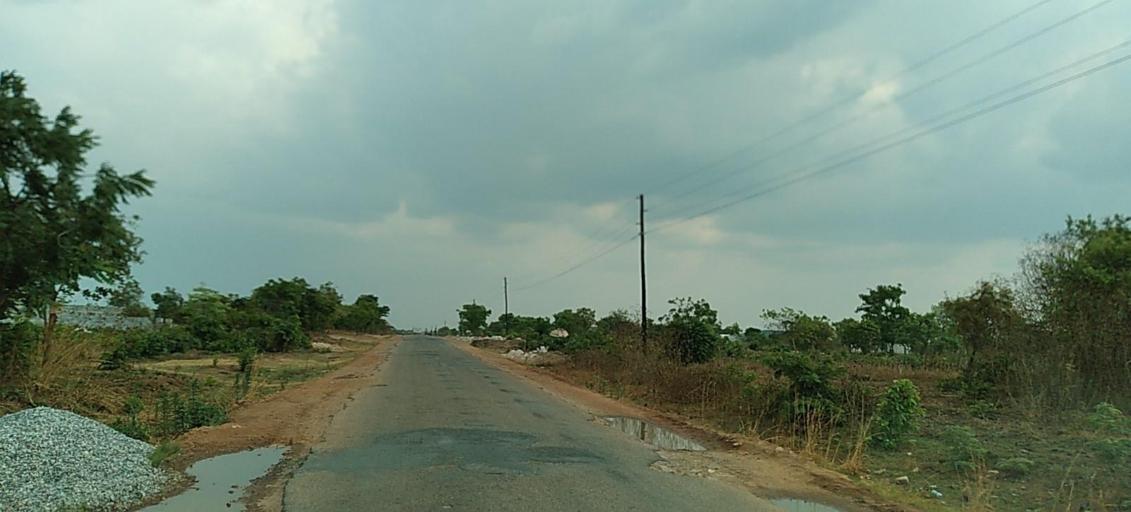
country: ZM
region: Copperbelt
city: Kalulushi
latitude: -12.8608
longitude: 28.1218
